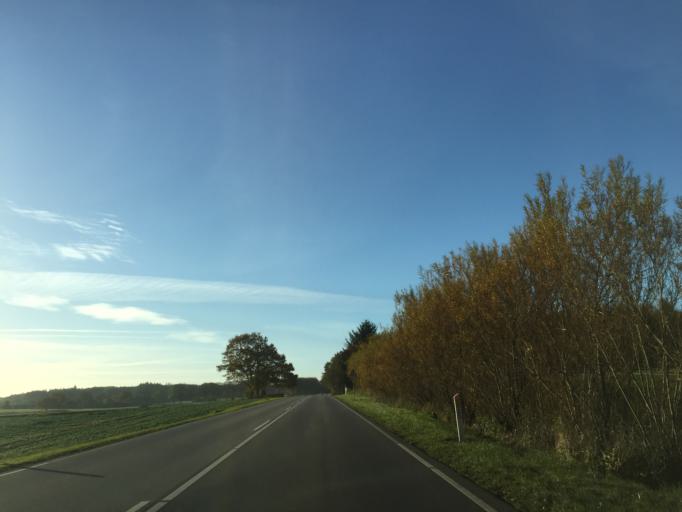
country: DK
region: Central Jutland
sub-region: Skanderborg Kommune
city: Skanderborg
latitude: 56.0893
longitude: 9.8988
